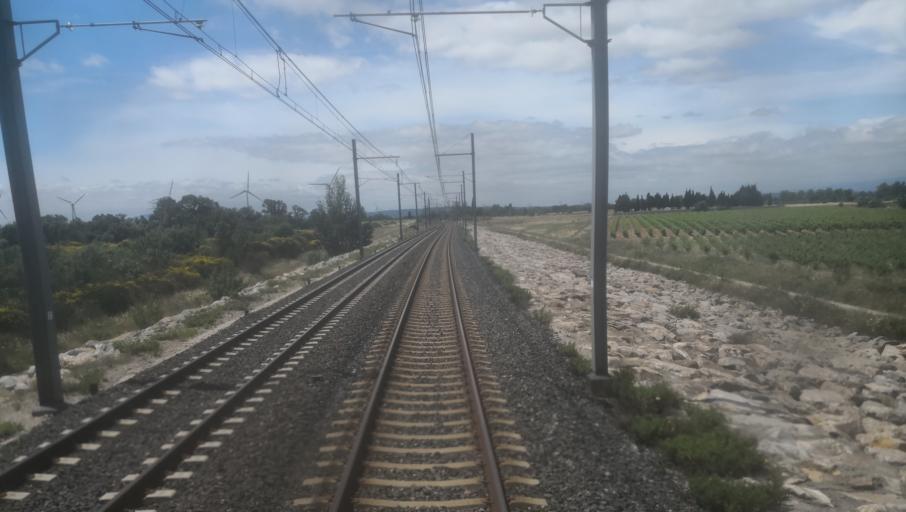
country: FR
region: Languedoc-Roussillon
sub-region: Departement de l'Aude
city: Canet
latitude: 43.2085
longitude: 2.8616
